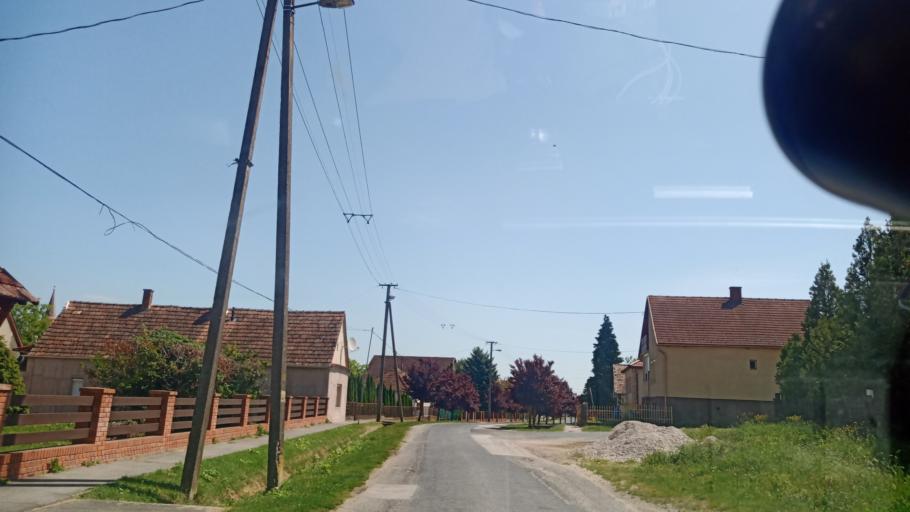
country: HU
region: Zala
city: Zalakomar
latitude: 46.6187
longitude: 17.1137
